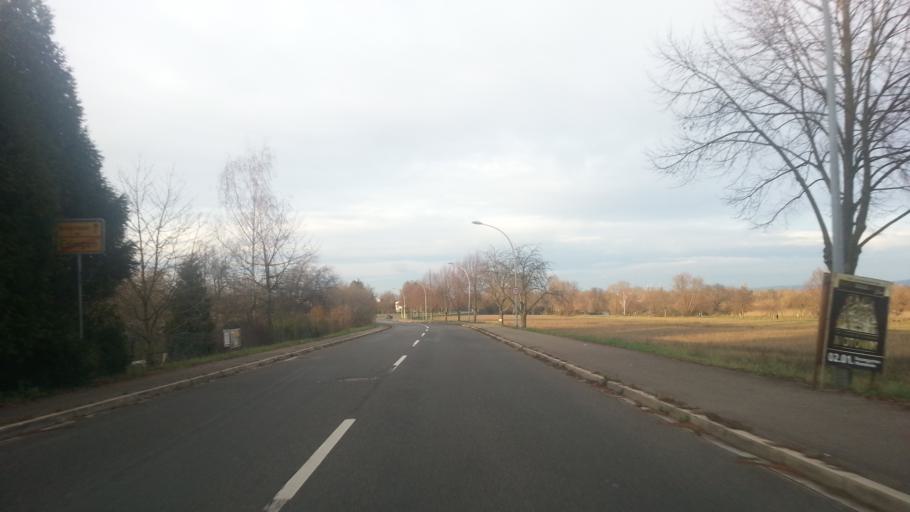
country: DE
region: Baden-Wuerttemberg
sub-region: Karlsruhe Region
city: Edingen-Neckarhausen
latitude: 49.4536
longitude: 8.6084
